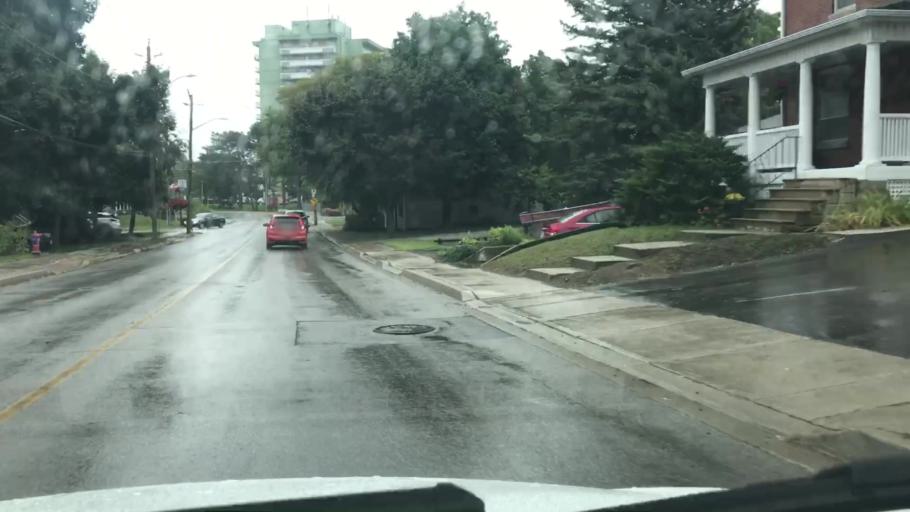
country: CA
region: Ontario
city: Newmarket
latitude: 44.0497
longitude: -79.4589
